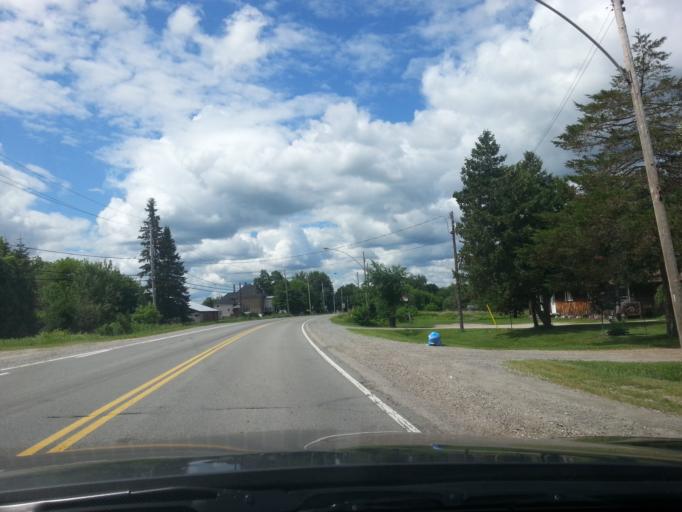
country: CA
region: Ontario
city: Perth
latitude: 44.7064
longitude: -76.1764
